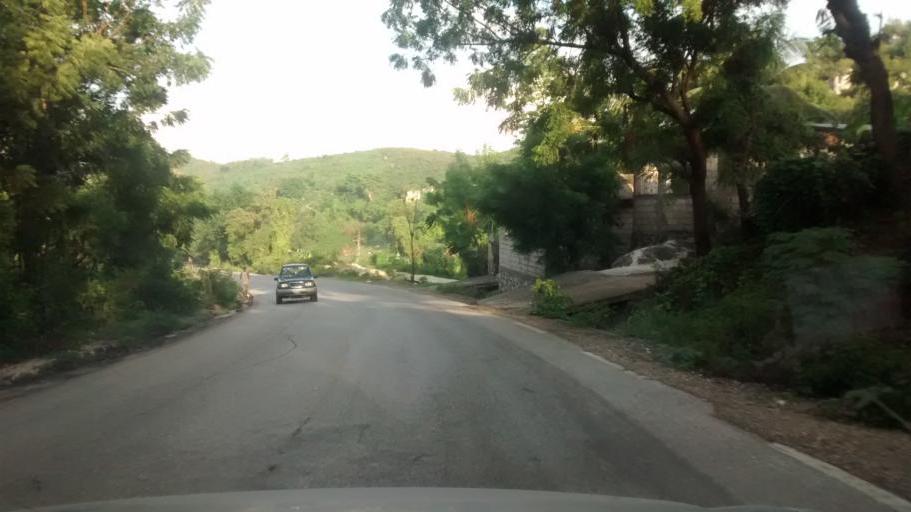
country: HT
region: Ouest
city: Tigwav
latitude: 18.4391
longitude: -72.8352
